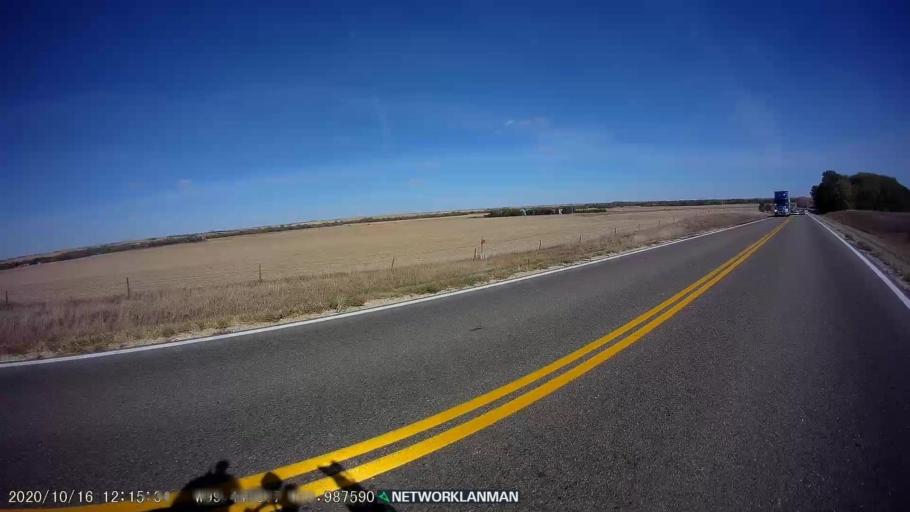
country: US
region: Nebraska
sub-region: Harlan County
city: Alma
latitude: 39.9880
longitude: -99.4455
